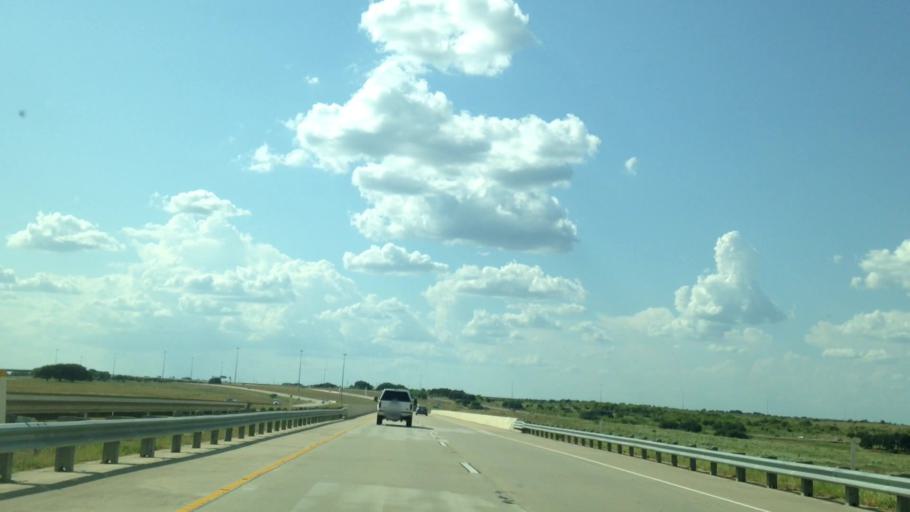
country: US
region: Texas
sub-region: Travis County
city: Onion Creek
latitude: 30.1063
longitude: -97.7883
